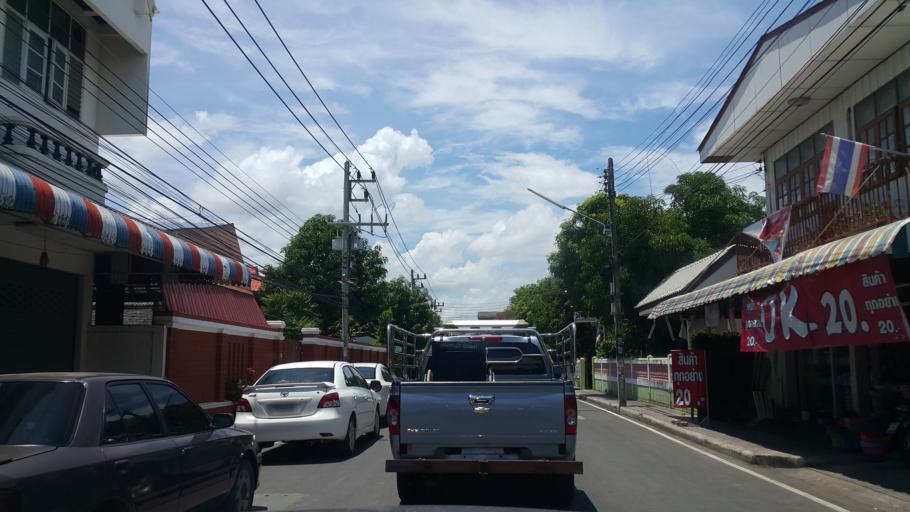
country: TH
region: Phayao
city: Phayao
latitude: 19.1660
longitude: 99.8982
